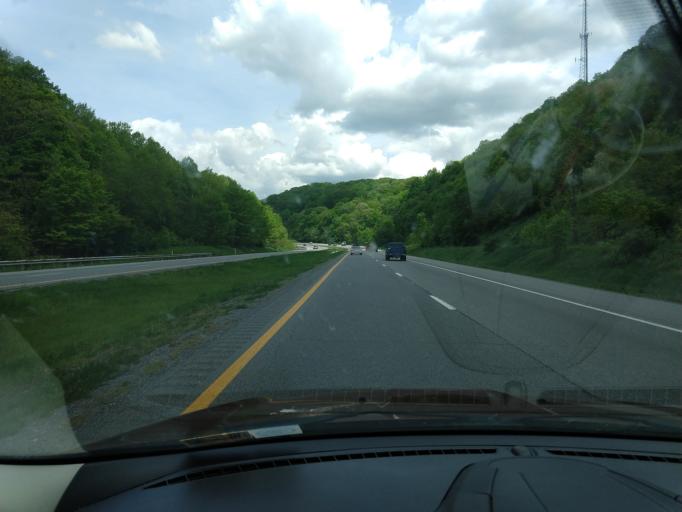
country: US
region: West Virginia
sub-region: Mercer County
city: Bluefield
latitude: 37.2965
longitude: -81.1573
